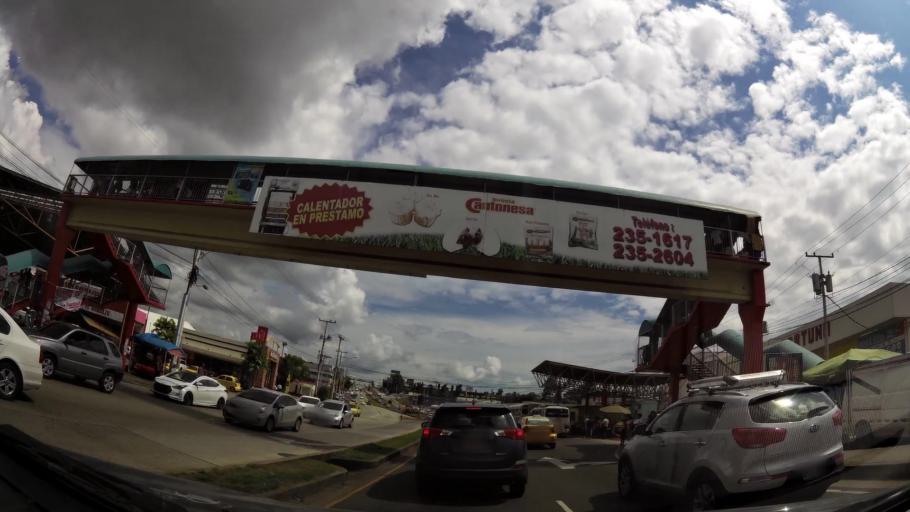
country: PA
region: Panama
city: Nuevo Arraijan
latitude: 8.9254
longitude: -79.7109
